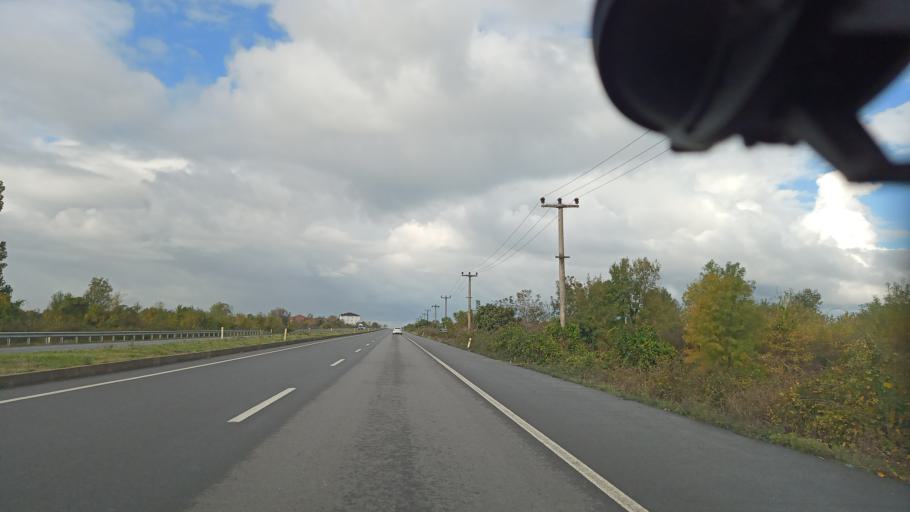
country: TR
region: Sakarya
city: Karasu
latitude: 41.0714
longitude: 30.7935
